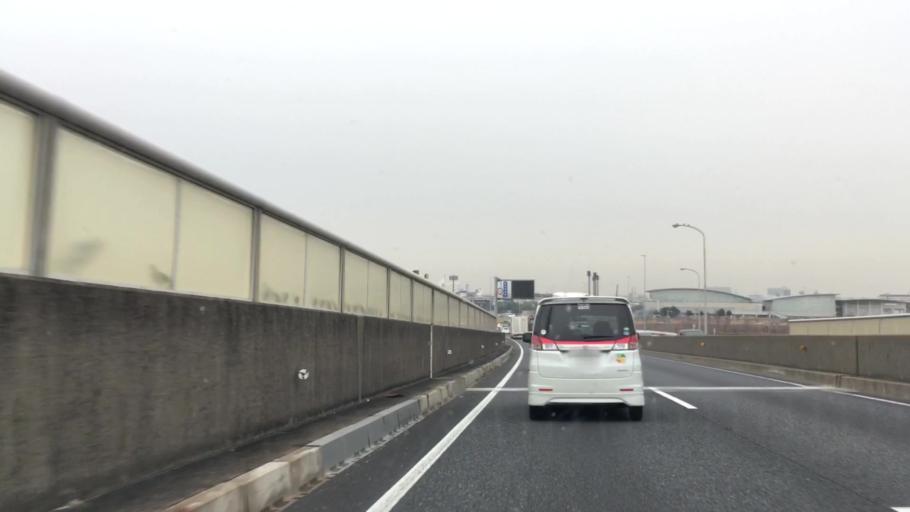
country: JP
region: Aichi
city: Chiryu
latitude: 35.0255
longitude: 137.0116
